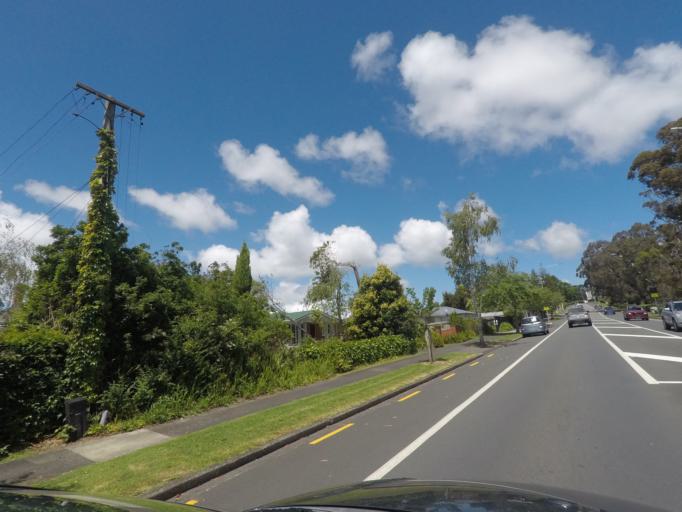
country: NZ
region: Auckland
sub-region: Auckland
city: Waitakere
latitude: -36.9056
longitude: 174.6531
